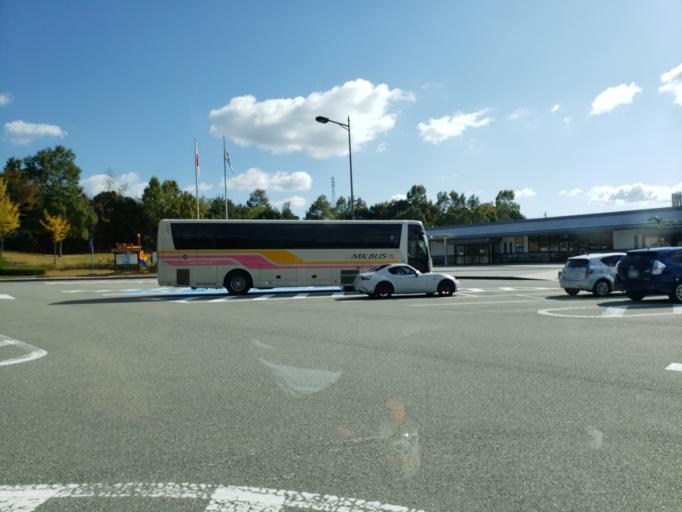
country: JP
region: Tokushima
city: Ishii
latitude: 34.1402
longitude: 134.4177
